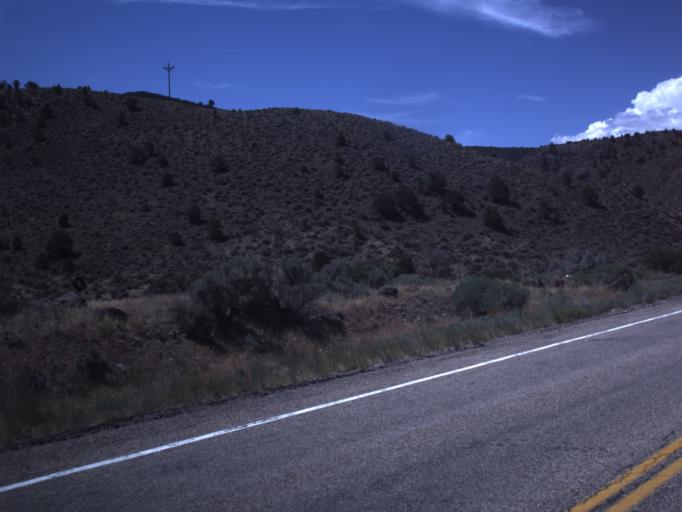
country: US
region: Utah
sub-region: Piute County
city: Junction
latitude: 38.1393
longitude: -112.3125
